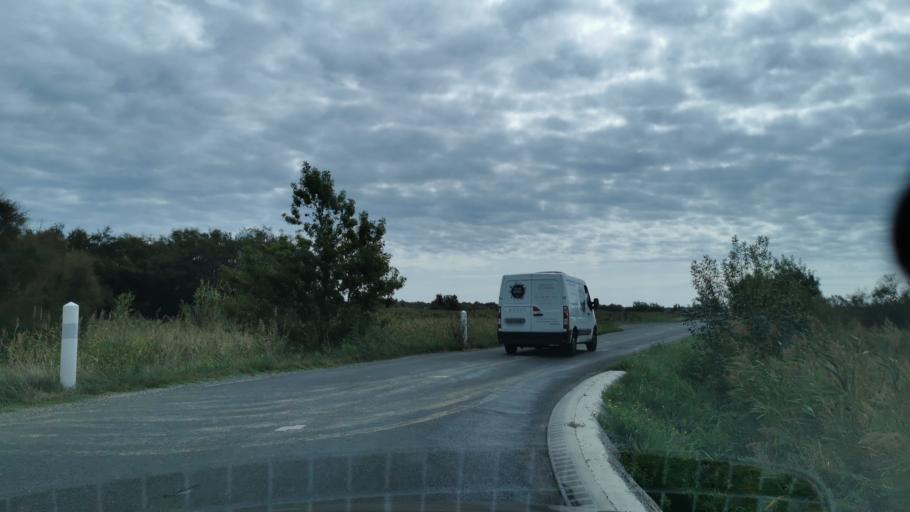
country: FR
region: Languedoc-Roussillon
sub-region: Departement de l'Herault
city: Vendres
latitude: 43.2301
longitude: 3.2039
